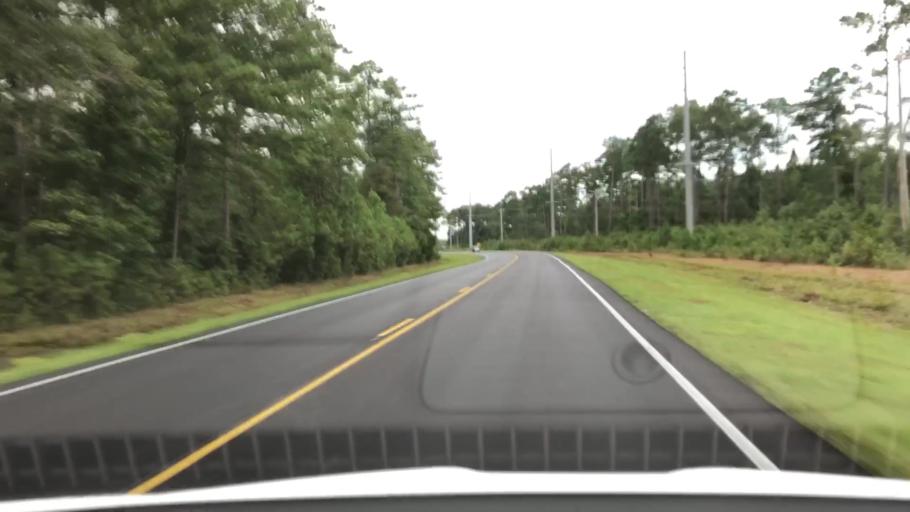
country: US
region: North Carolina
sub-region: Onslow County
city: Swansboro
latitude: 34.7855
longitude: -77.1171
